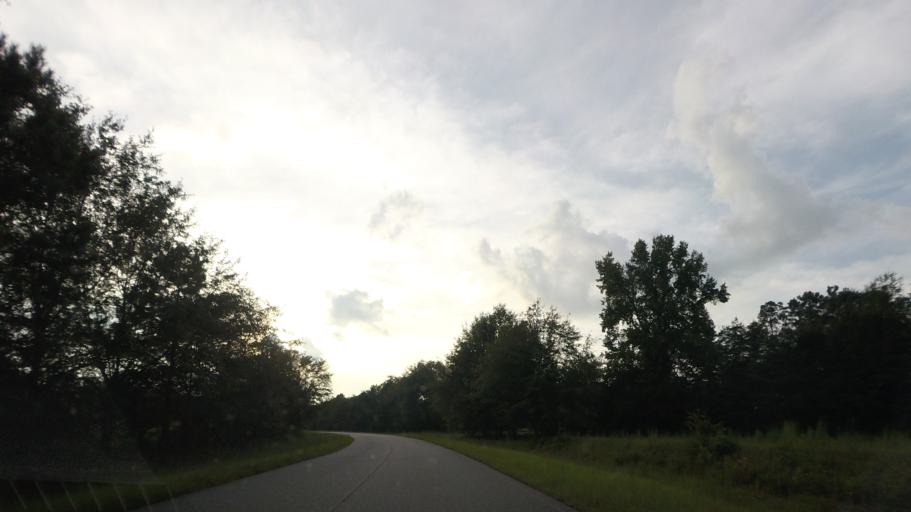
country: US
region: Georgia
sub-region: Wilkinson County
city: Gordon
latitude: 32.8688
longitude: -83.4724
